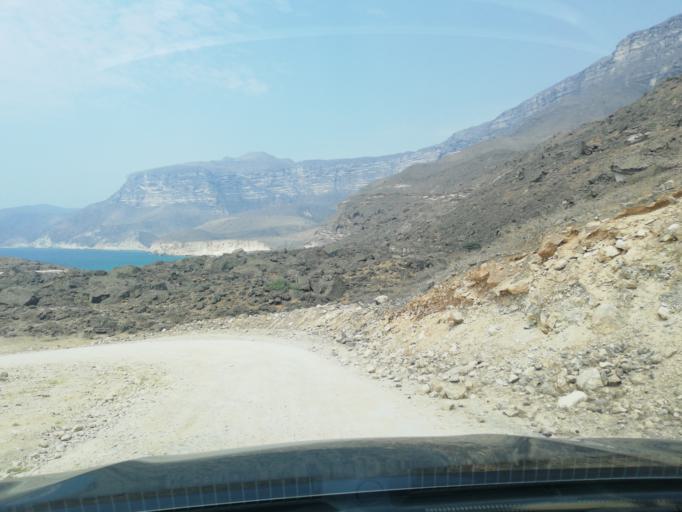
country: OM
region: Zufar
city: Salalah
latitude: 16.8192
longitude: 53.6946
